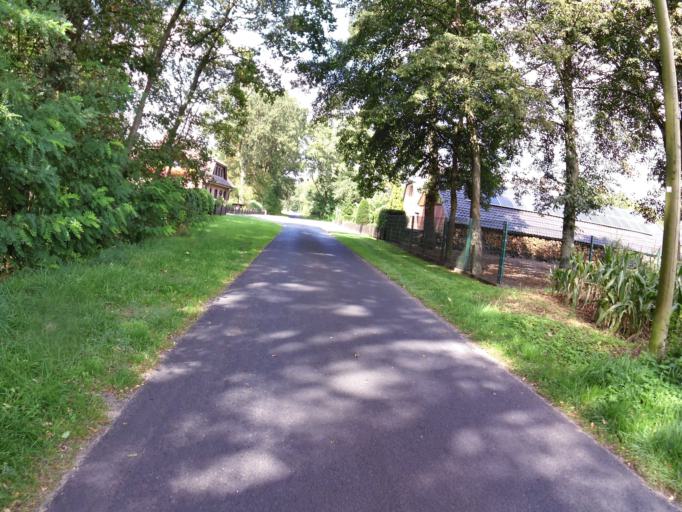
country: DE
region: North Rhine-Westphalia
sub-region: Regierungsbezirk Munster
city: Gronau
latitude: 52.1643
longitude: 7.0110
